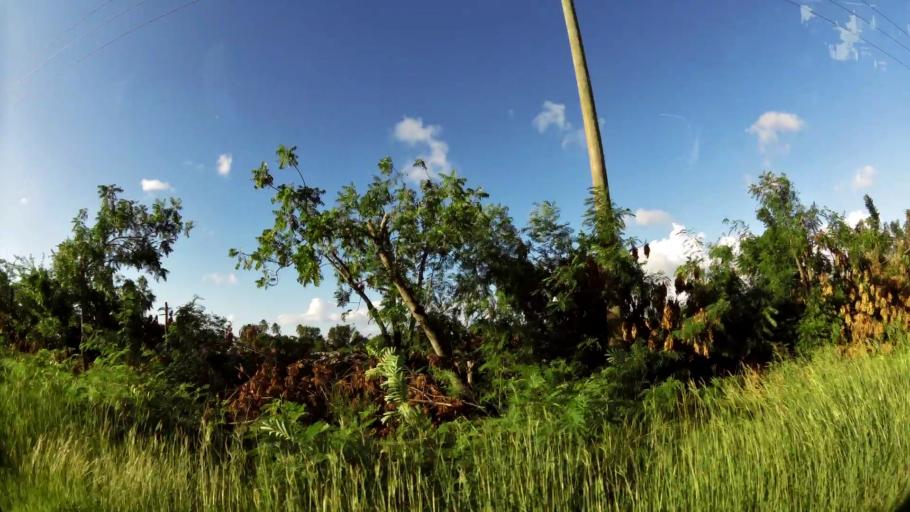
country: GD
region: Saint George
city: Saint George's
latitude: 12.0206
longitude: -61.7643
